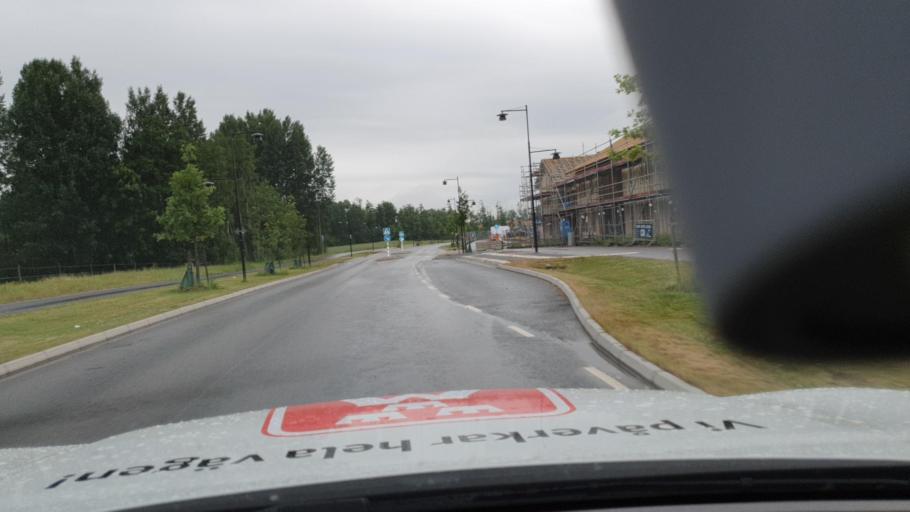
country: SE
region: Vaestra Goetaland
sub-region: Skovde Kommun
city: Stopen
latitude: 58.4203
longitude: 13.9008
